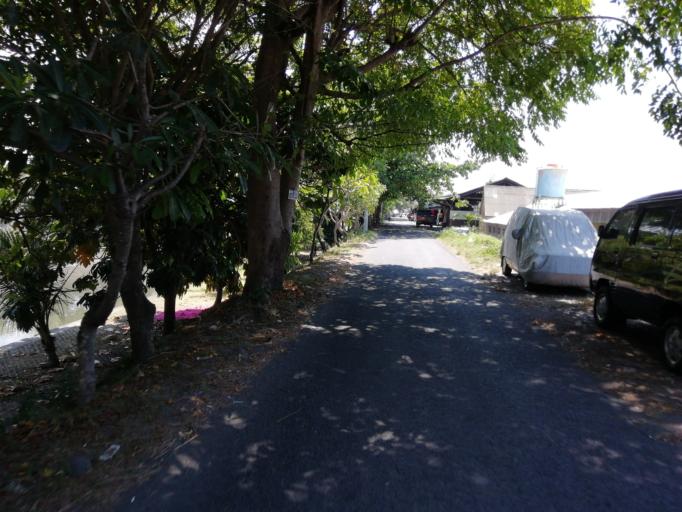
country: ID
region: Bali
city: Karyadharma
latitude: -8.6921
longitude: 115.1973
